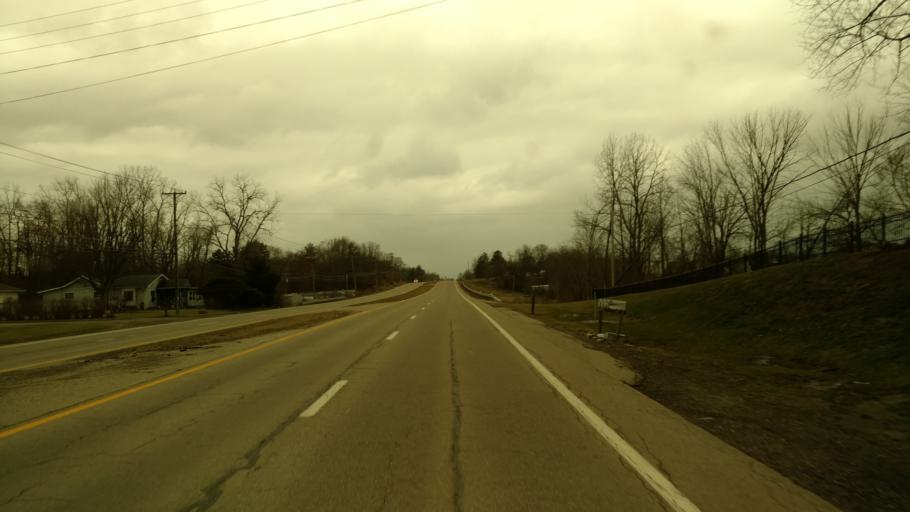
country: US
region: Ohio
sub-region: Licking County
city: Etna
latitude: 39.9583
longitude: -82.6384
